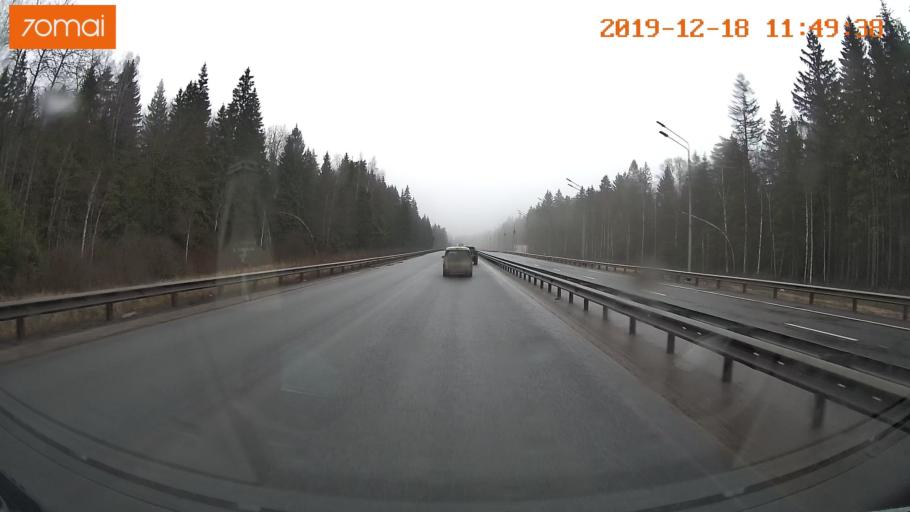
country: RU
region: Moskovskaya
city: Yershovo
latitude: 55.7792
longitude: 36.9130
